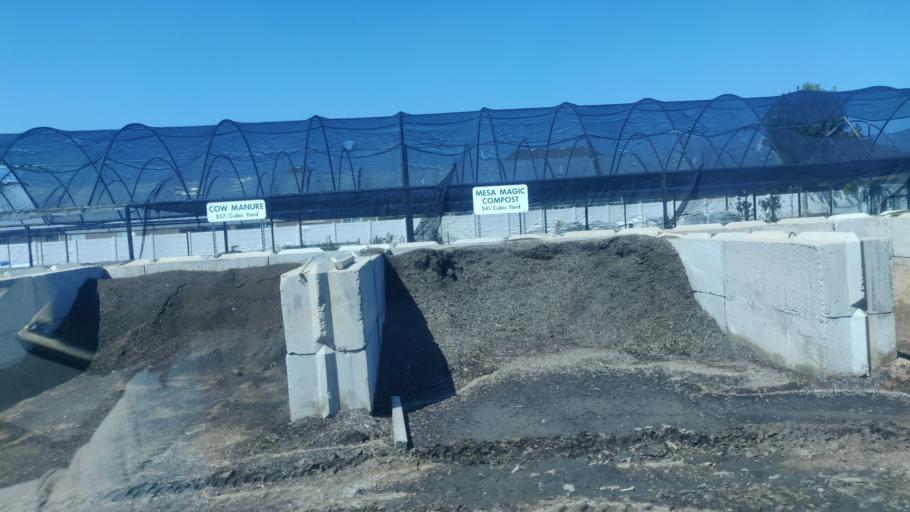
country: US
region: Colorado
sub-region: Mesa County
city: Clifton
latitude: 39.0939
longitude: -108.4660
